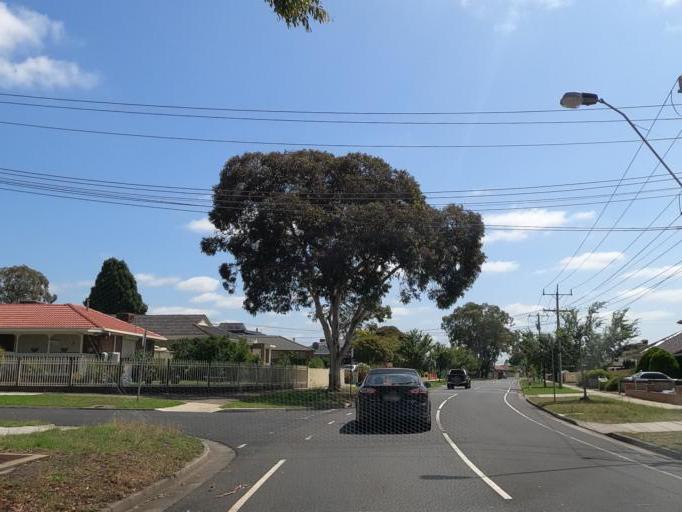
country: AU
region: Victoria
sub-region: Hume
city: Gladstone Park
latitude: -37.6944
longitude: 144.8940
